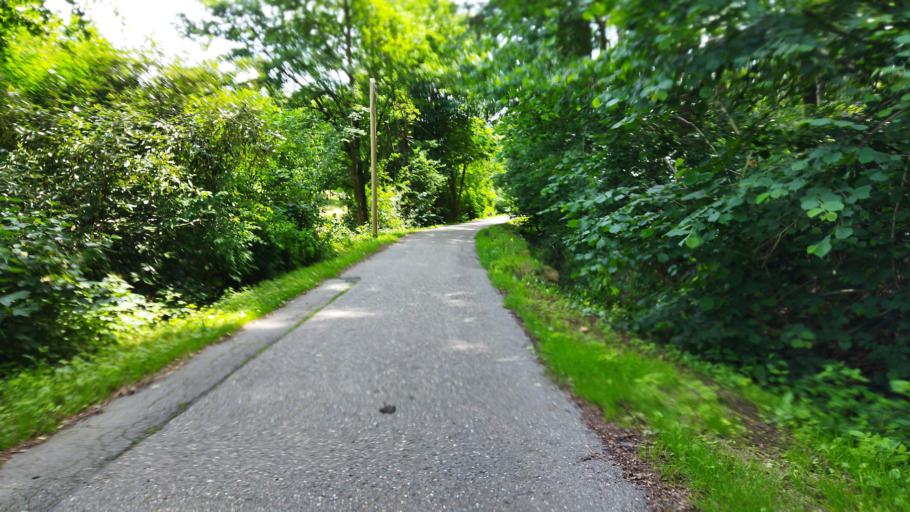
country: DE
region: Baden-Wuerttemberg
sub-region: Regierungsbezirk Stuttgart
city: Zaberfeld
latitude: 49.0708
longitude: 8.8883
